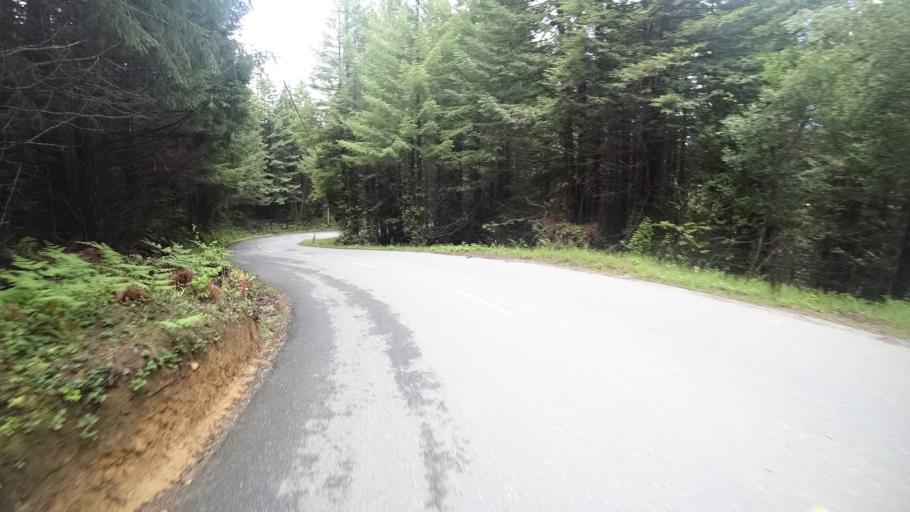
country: US
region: California
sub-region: Humboldt County
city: Blue Lake
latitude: 40.8708
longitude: -123.9548
